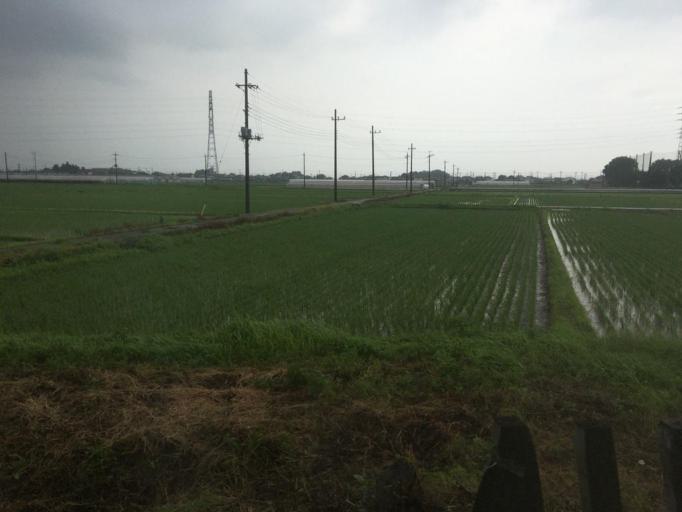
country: JP
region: Tochigi
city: Ashikaga
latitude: 36.2944
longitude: 139.4660
